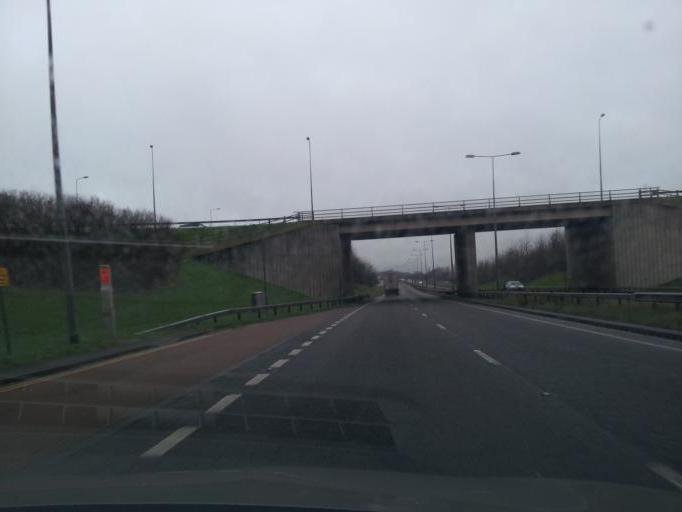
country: GB
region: England
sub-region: Derbyshire
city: Melbourne
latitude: 52.8605
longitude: -1.4395
